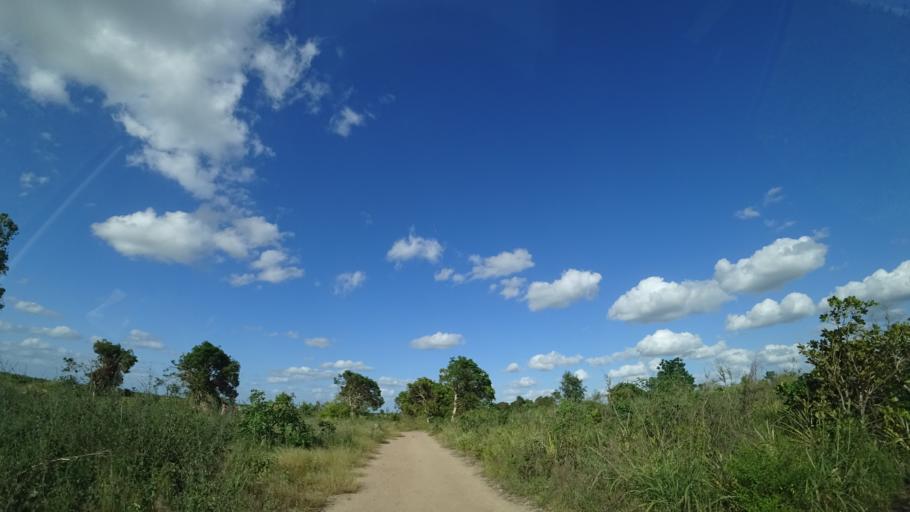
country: MZ
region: Sofala
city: Dondo
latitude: -19.4311
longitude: 34.7296
